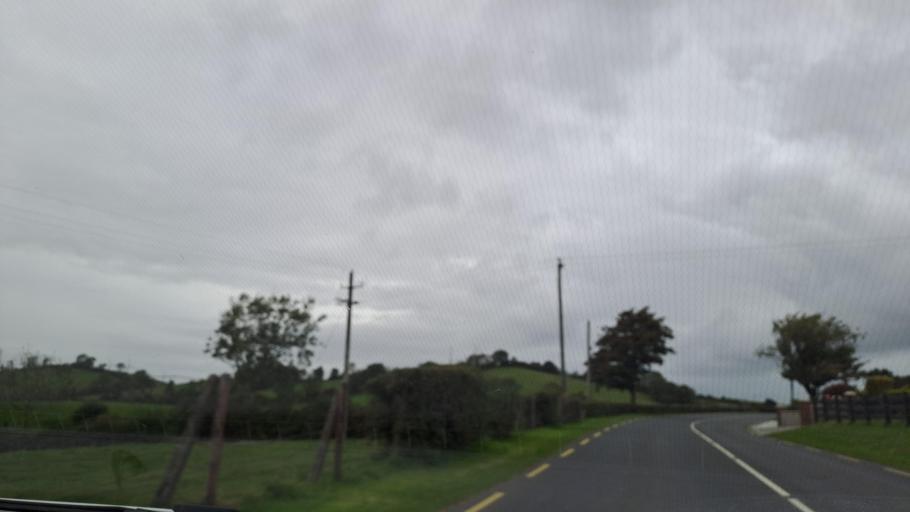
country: IE
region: Ulster
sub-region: County Monaghan
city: Castleblayney
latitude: 54.0743
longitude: -6.8224
